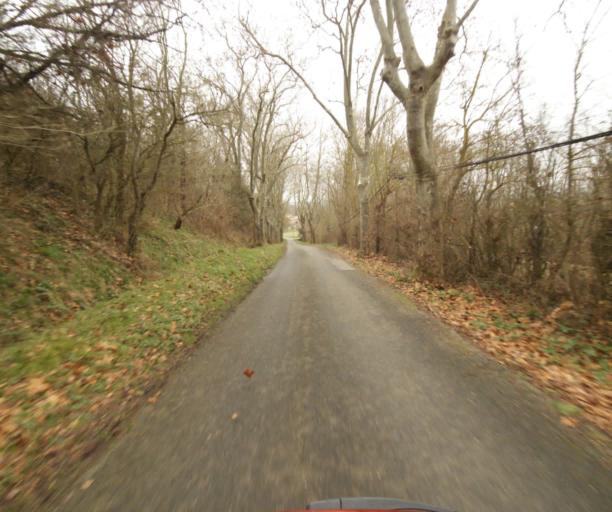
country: FR
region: Midi-Pyrenees
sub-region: Departement de la Haute-Garonne
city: Gaillac-Toulza
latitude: 43.2649
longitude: 1.5133
